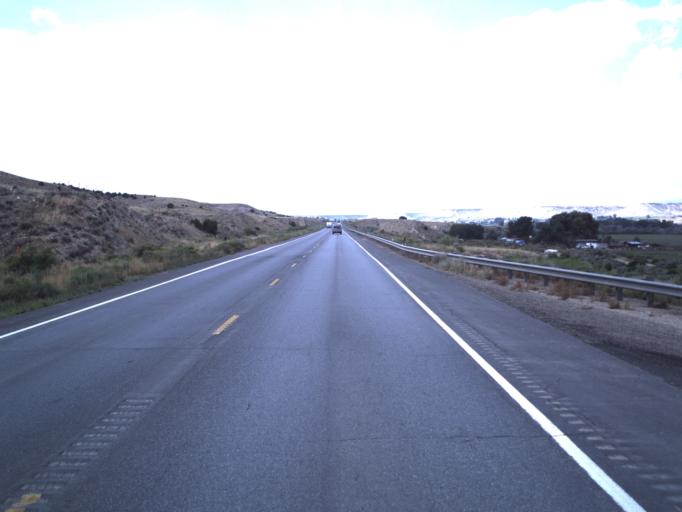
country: US
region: Utah
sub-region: Duchesne County
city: Duchesne
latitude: 40.1618
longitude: -110.2748
